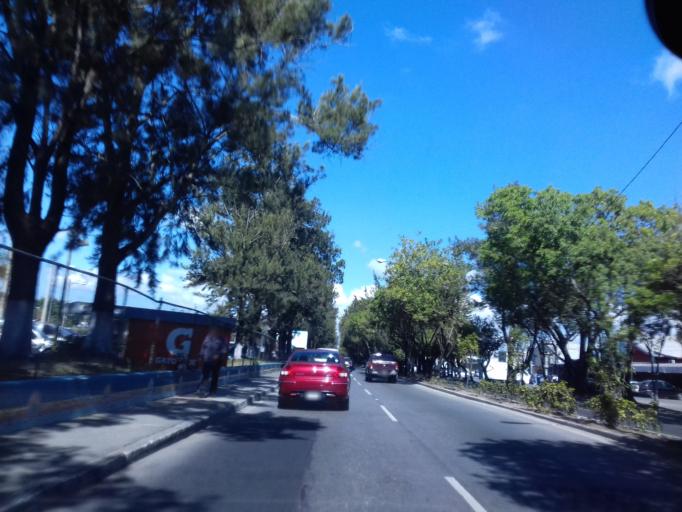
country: GT
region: Guatemala
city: Guatemala City
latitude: 14.6148
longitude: -90.5051
